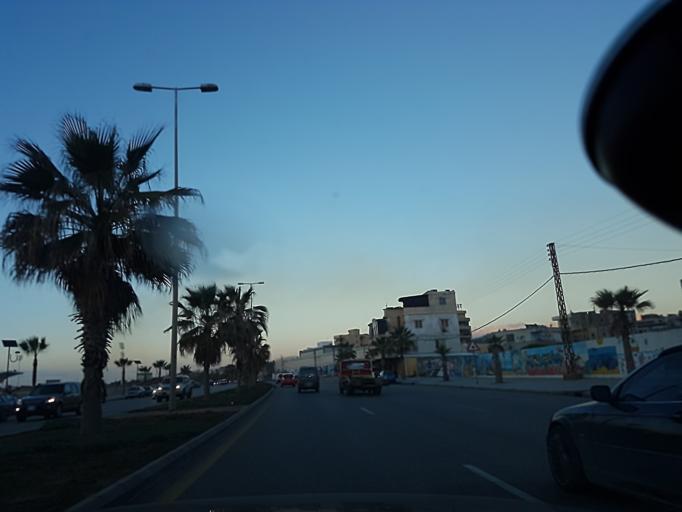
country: LB
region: Liban-Sud
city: Sidon
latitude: 33.5787
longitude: 35.3835
